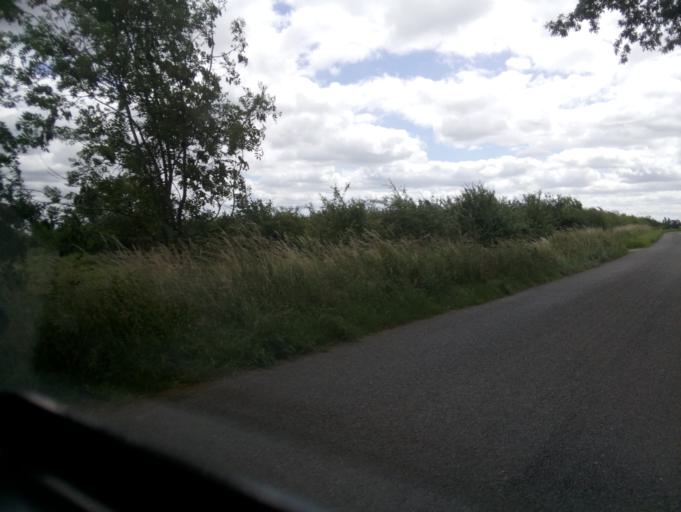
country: GB
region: England
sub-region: Nottinghamshire
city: Ruddington
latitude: 52.8460
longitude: -1.1031
